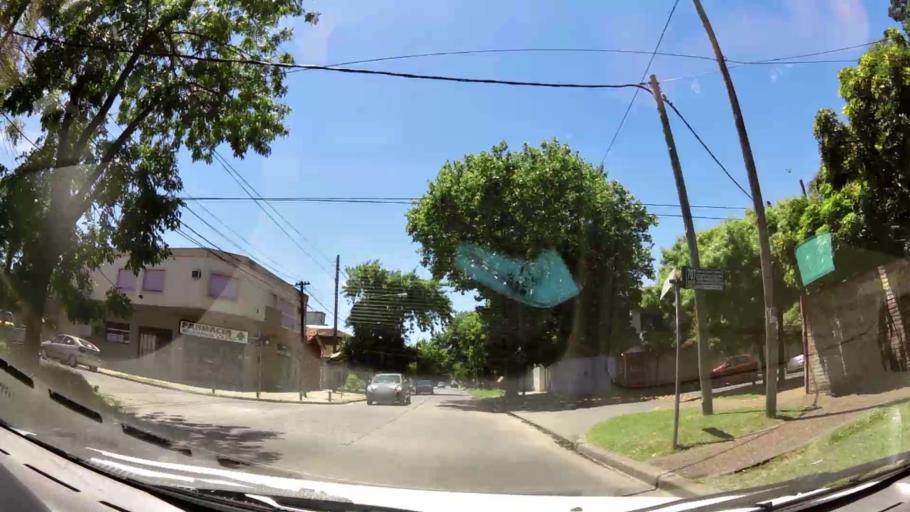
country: AR
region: Buenos Aires
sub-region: Partido de Vicente Lopez
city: Olivos
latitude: -34.5023
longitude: -58.5197
